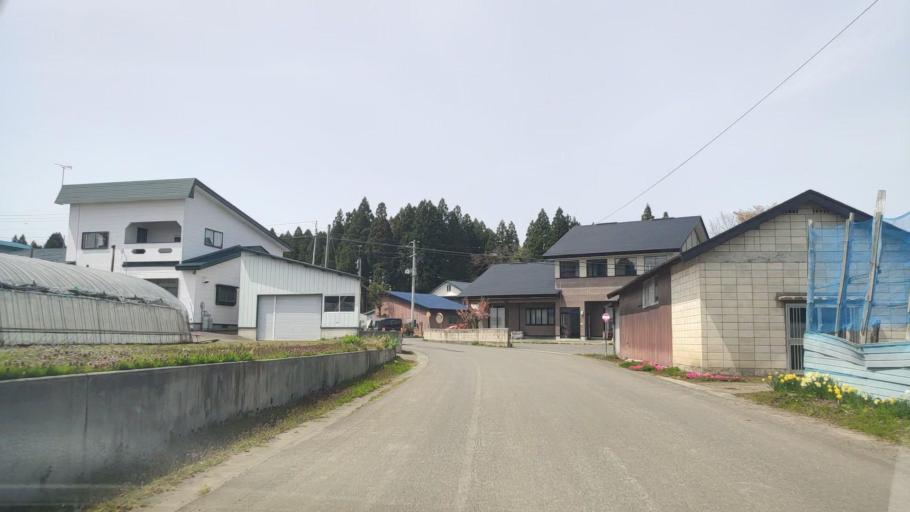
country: JP
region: Aomori
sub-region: Misawa Shi
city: Inuotose
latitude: 40.7799
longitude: 141.1217
